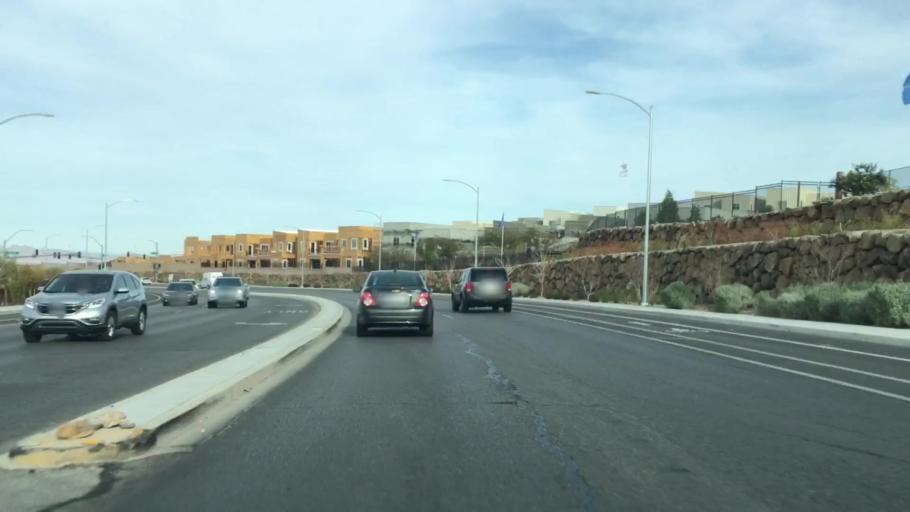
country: US
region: Nevada
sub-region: Clark County
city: Whitney
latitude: 35.9987
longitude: -115.0843
